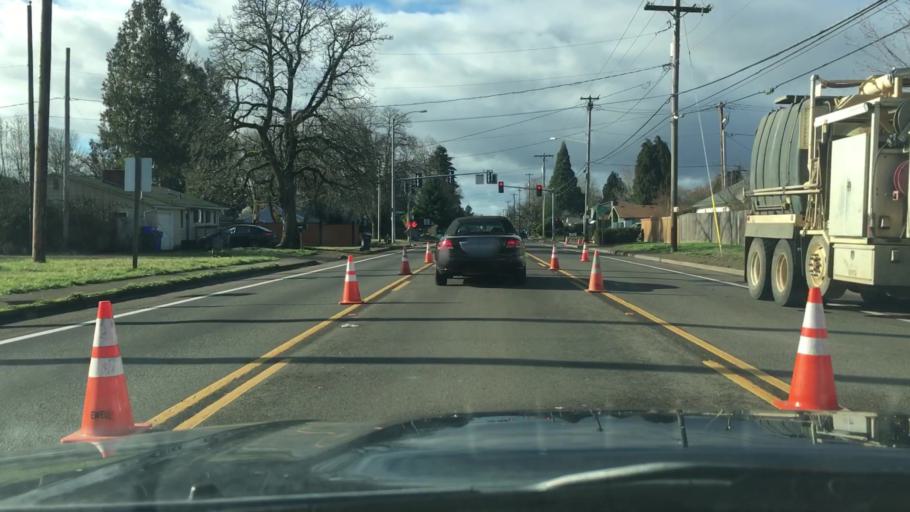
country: US
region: Oregon
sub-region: Lane County
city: Eugene
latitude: 44.0700
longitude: -123.1670
